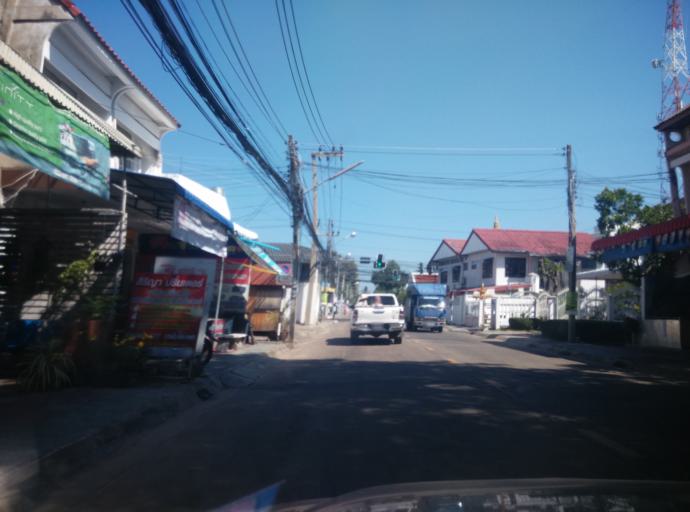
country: TH
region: Sisaket
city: Si Sa Ket
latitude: 15.1181
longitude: 104.3229
